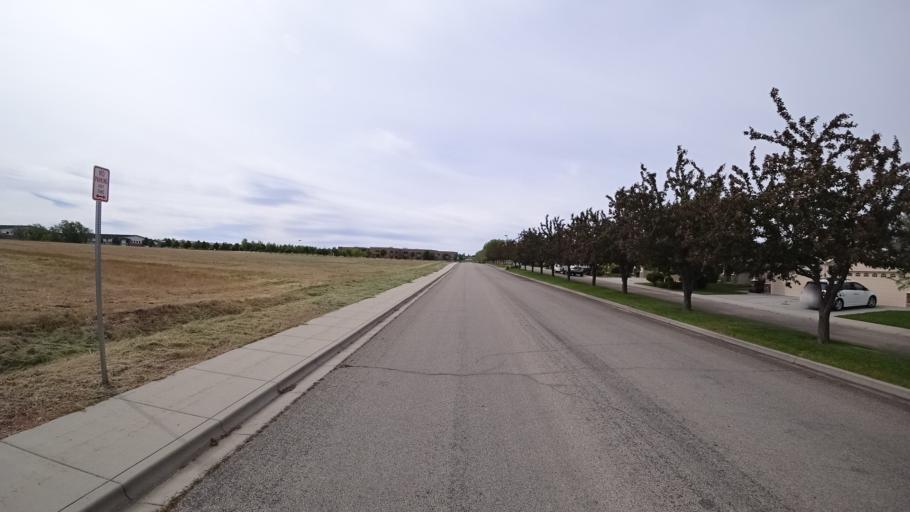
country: US
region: Idaho
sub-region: Ada County
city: Garden City
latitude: 43.5743
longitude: -116.2866
